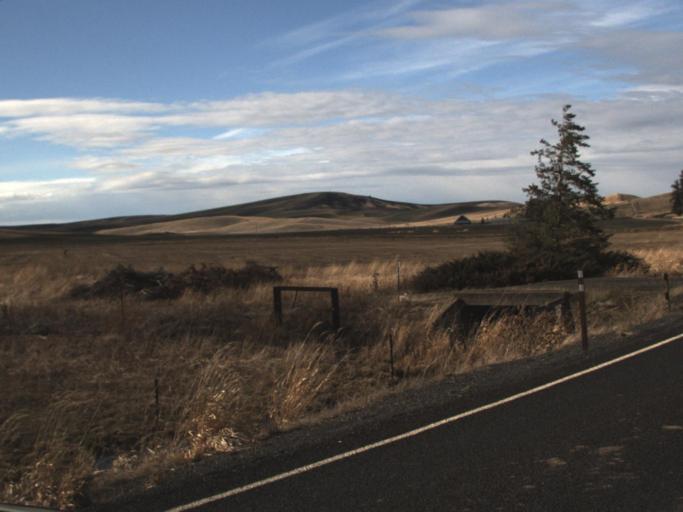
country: US
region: Washington
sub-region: Whitman County
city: Pullman
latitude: 46.9320
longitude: -117.1254
